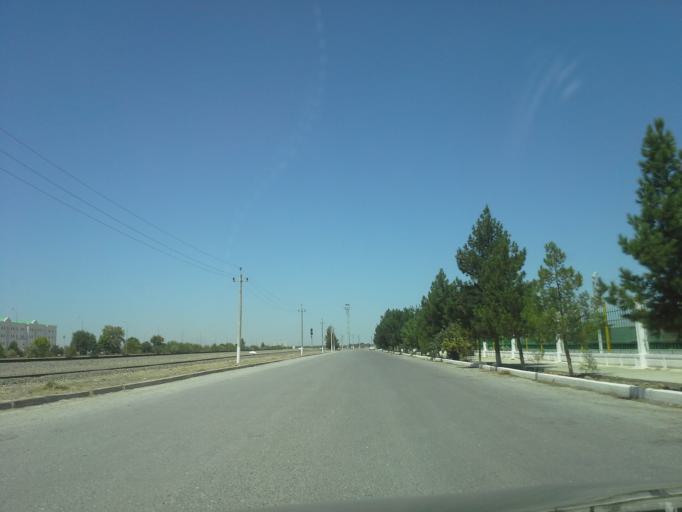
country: TM
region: Ahal
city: Ashgabat
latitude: 37.9933
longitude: 58.3167
